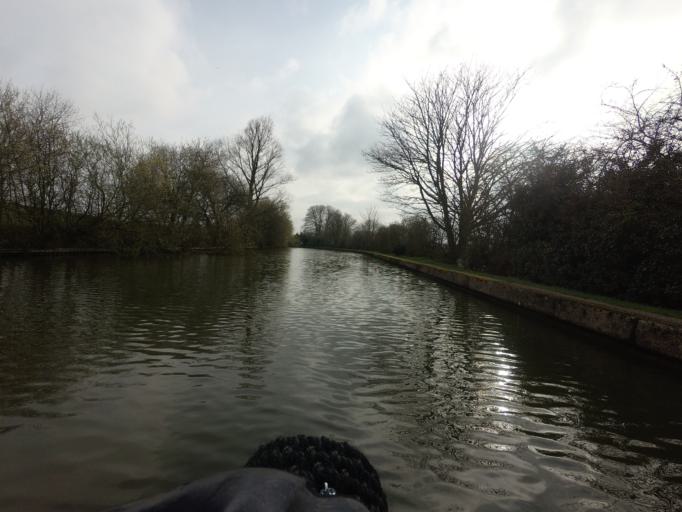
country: GB
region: England
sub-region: Buckinghamshire
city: Cheddington
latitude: 51.8276
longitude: -0.6624
